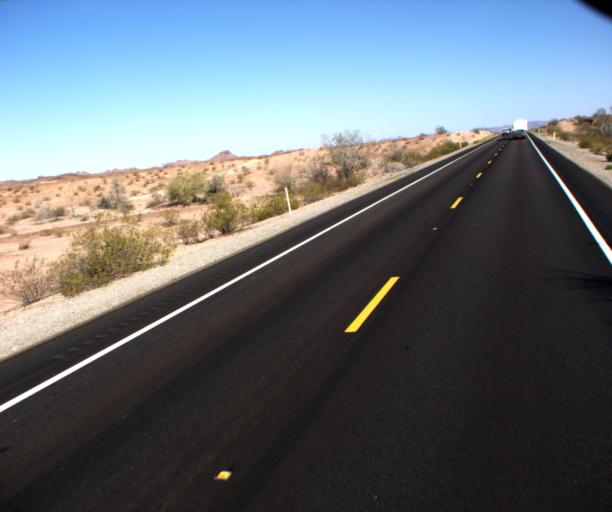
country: US
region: Arizona
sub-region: Yuma County
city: Wellton
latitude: 33.0508
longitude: -114.2913
